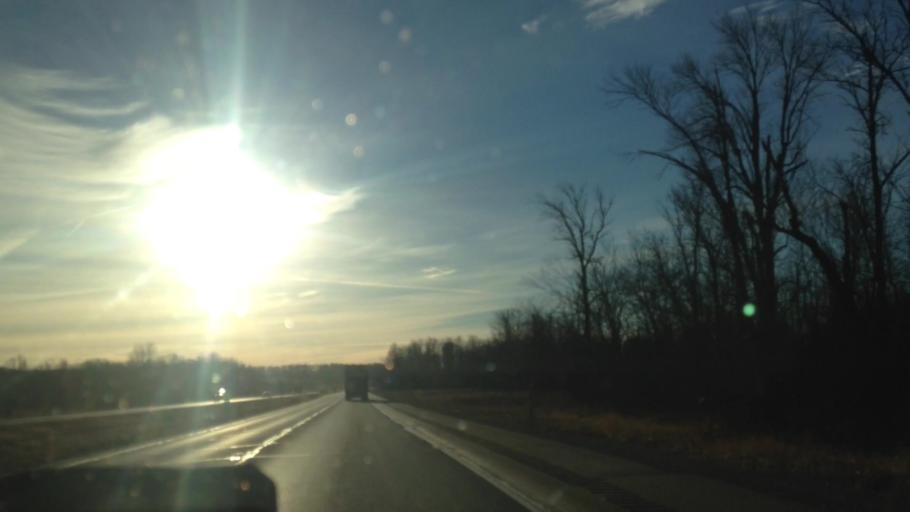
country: US
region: Wisconsin
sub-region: Washington County
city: Slinger
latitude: 43.4412
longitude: -88.3489
